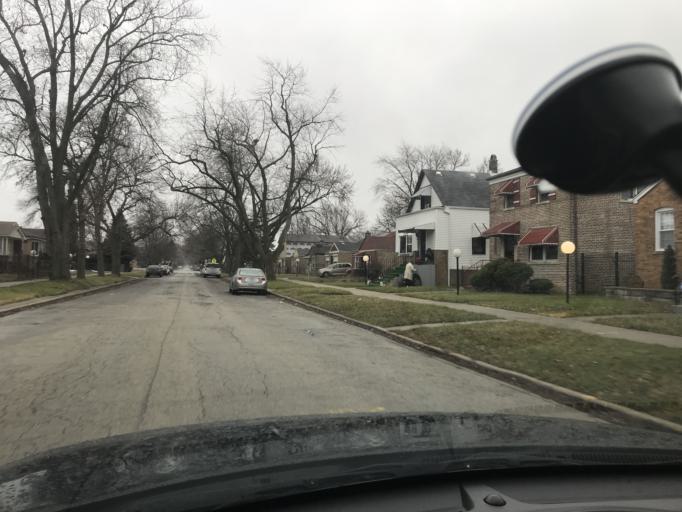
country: US
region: Illinois
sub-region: Cook County
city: Evergreen Park
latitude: 41.7266
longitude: -87.6397
